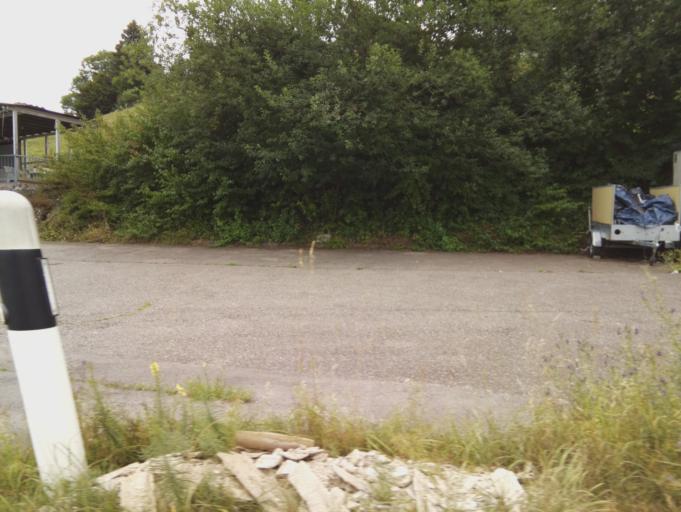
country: CH
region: Saint Gallen
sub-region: Wahlkreis Toggenburg
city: Lutisburg
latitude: 47.4083
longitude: 9.0815
